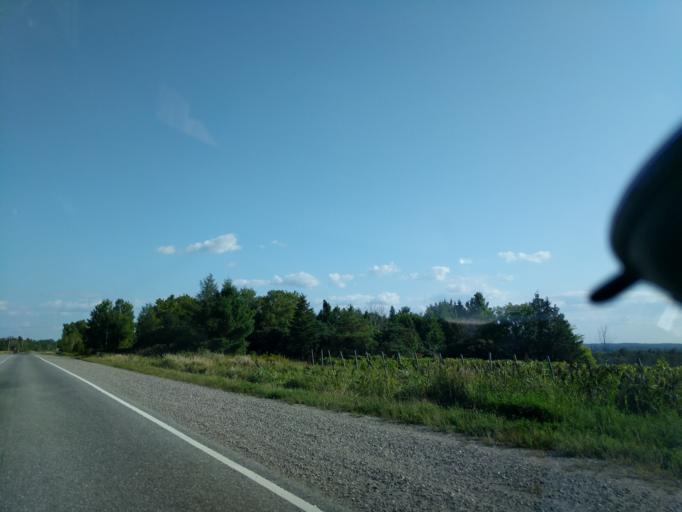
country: CA
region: Quebec
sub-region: Outaouais
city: Wakefield
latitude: 45.5184
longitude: -75.9859
